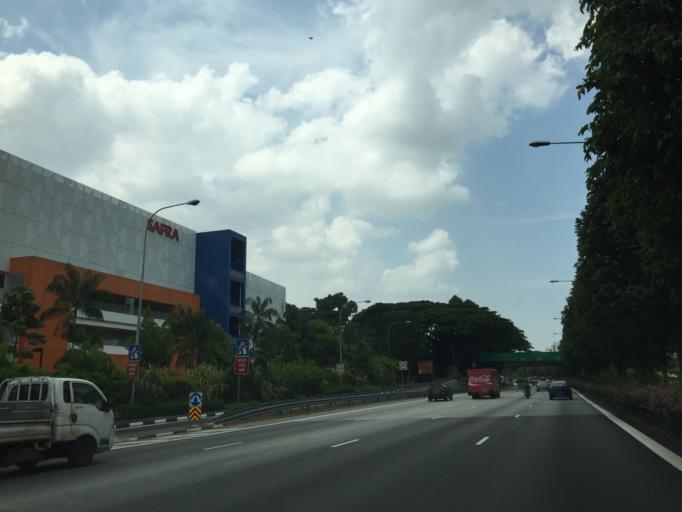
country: SG
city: Singapore
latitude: 1.3293
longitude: 103.8538
